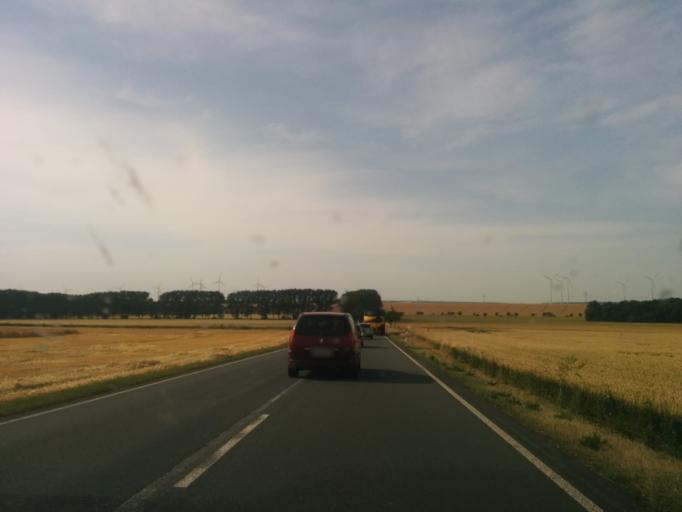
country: DE
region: Thuringia
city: Straussfurt
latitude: 51.1801
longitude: 10.9843
